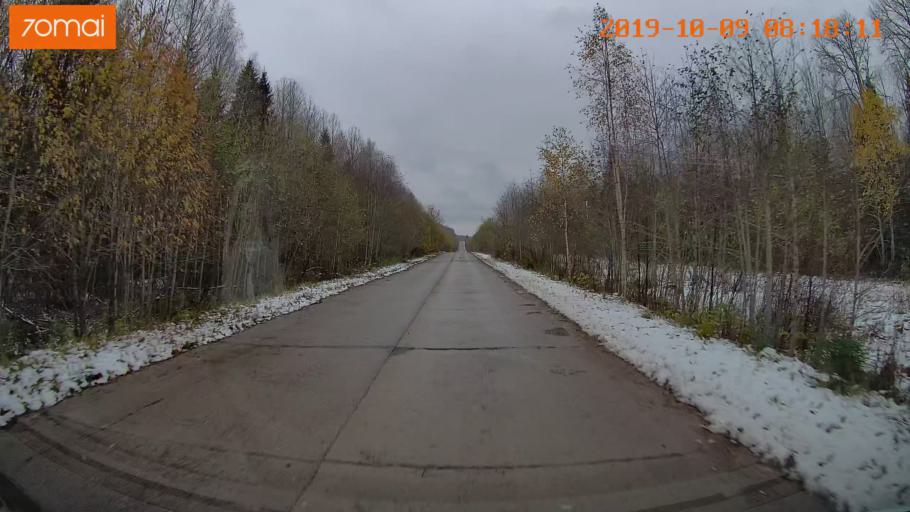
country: RU
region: Vologda
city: Gryazovets
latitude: 58.7399
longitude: 40.2191
